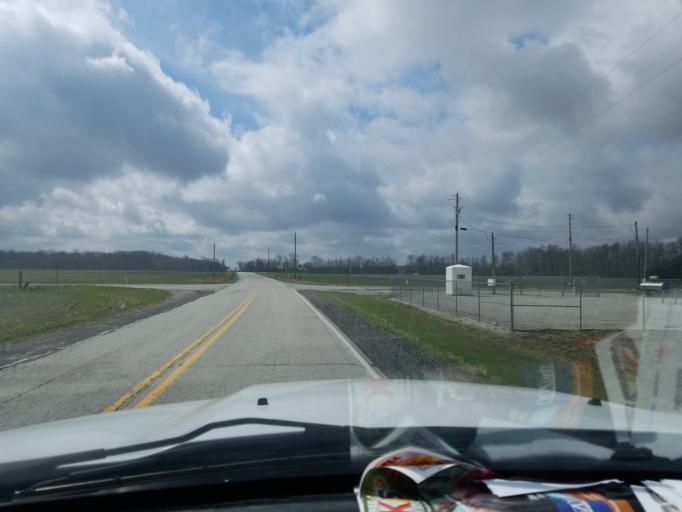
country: US
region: Indiana
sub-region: Sullivan County
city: Farmersburg
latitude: 39.3473
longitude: -87.3102
